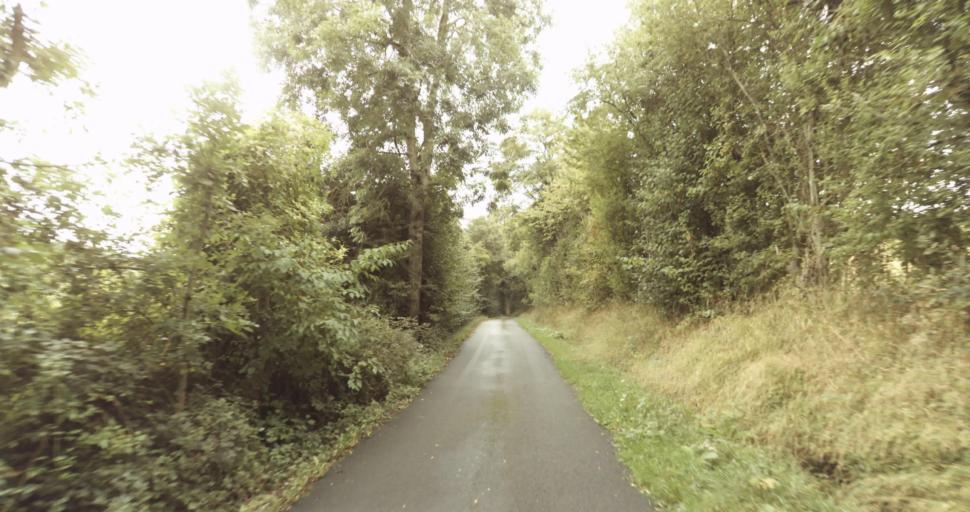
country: FR
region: Lower Normandy
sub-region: Departement de l'Orne
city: Vimoutiers
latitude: 48.8764
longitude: 0.2146
